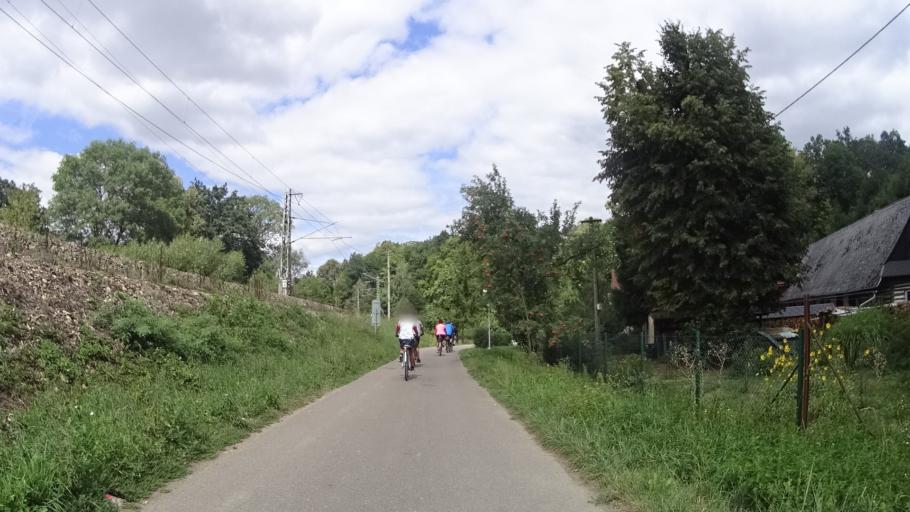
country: CZ
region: Pardubicky
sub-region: Okres Usti nad Orlici
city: Usti nad Orlici
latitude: 49.9877
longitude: 16.4014
